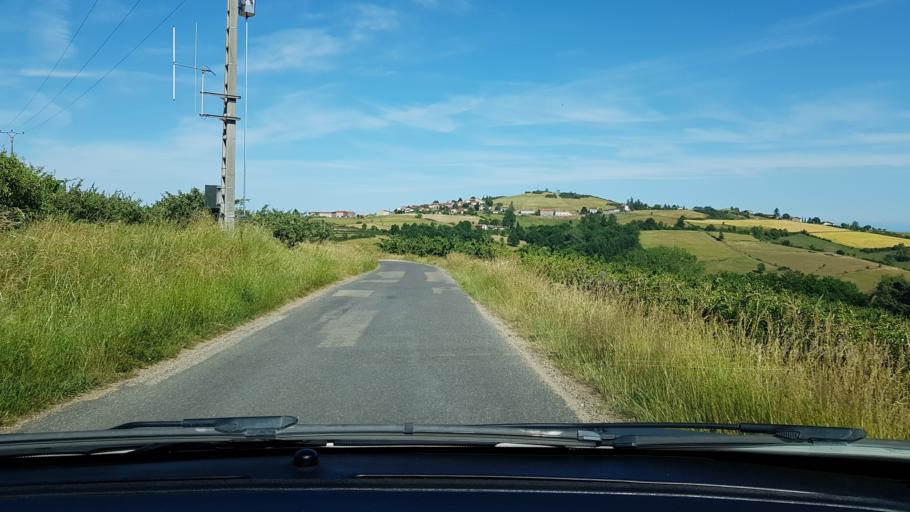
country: FR
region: Rhone-Alpes
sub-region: Departement du Rhone
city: Saint-Didier-sous-Riverie
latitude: 45.5916
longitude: 4.6007
